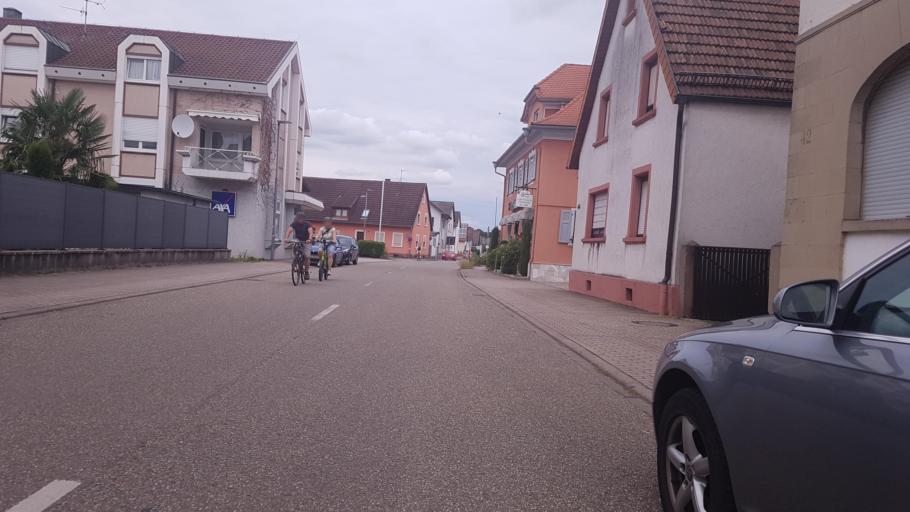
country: DE
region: Baden-Wuerttemberg
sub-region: Karlsruhe Region
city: Otigheim
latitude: 48.8911
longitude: 8.2349
